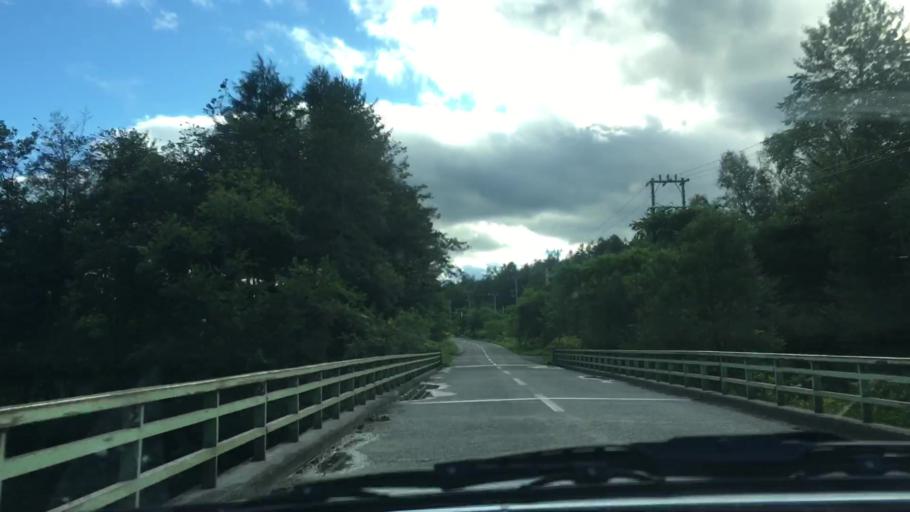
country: JP
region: Hokkaido
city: Otofuke
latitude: 43.1721
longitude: 142.9152
